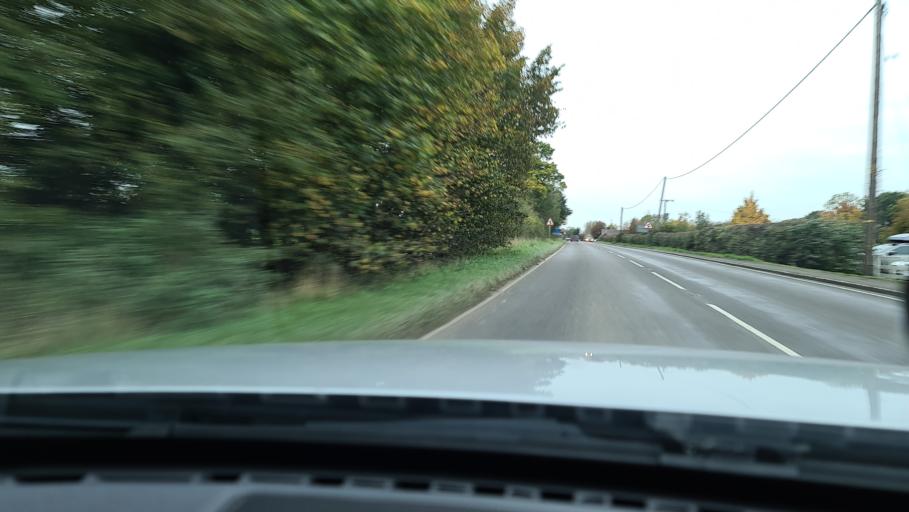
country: GB
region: England
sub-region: Buckinghamshire
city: Steeple Claydon
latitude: 51.8640
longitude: -0.9941
